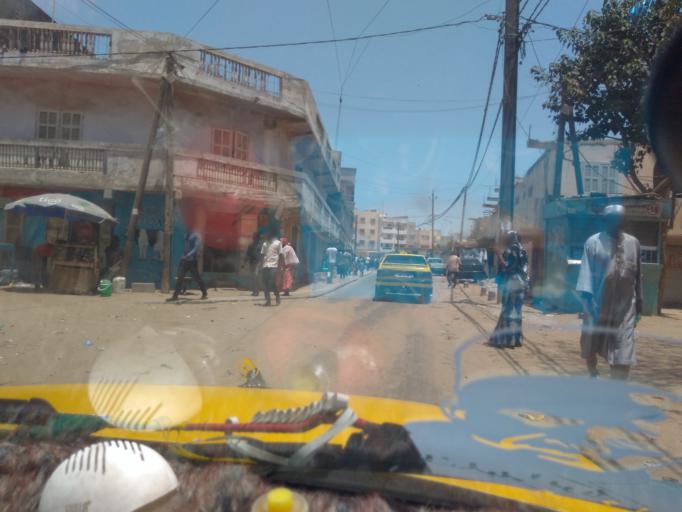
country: SN
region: Dakar
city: Grand Dakar
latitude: 14.7417
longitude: -17.4490
